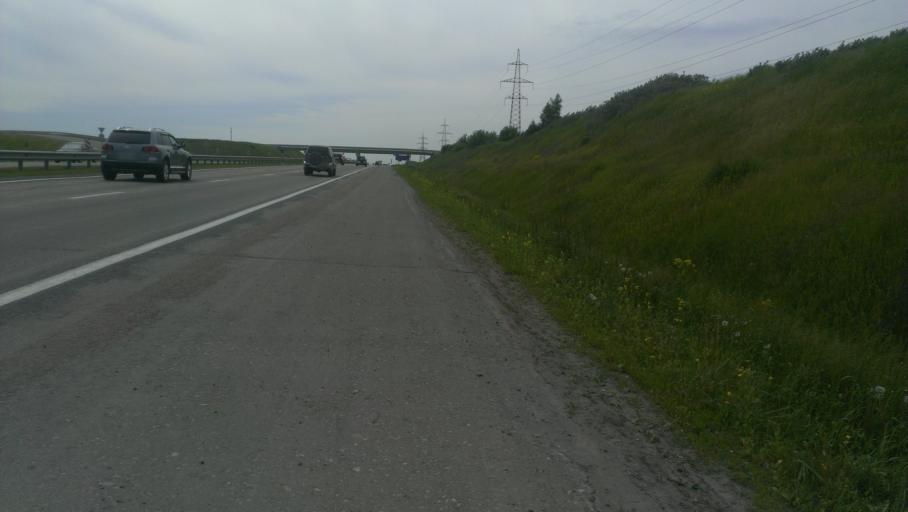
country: RU
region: Altai Krai
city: Sannikovo
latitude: 53.3432
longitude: 83.9397
